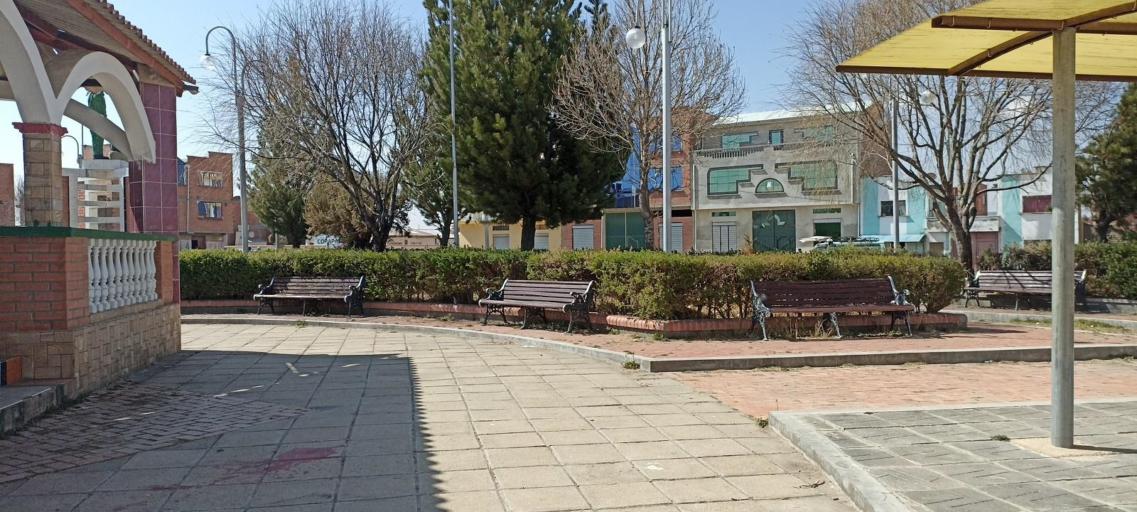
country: BO
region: La Paz
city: Batallas
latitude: -16.4376
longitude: -68.3733
